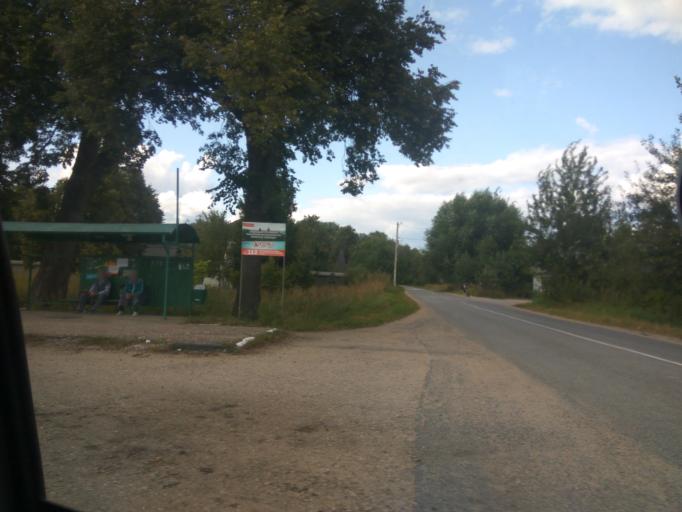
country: RU
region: Moskovskaya
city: Bronnitsy
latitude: 55.4581
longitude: 38.2314
